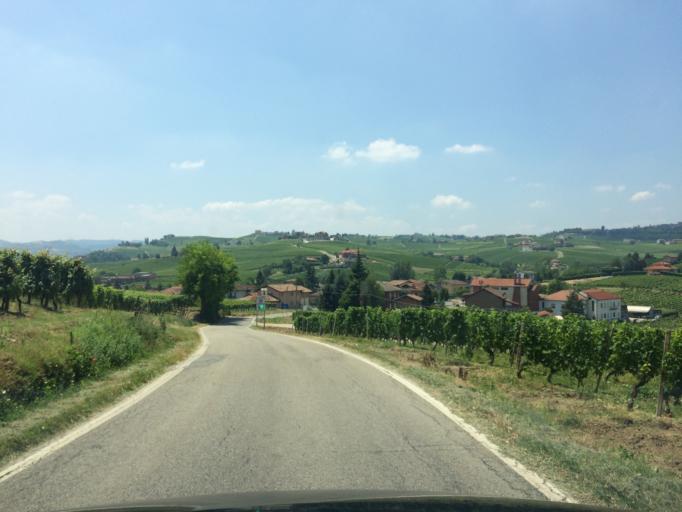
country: IT
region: Piedmont
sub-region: Provincia di Asti
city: Calosso
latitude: 44.7485
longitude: 8.2542
